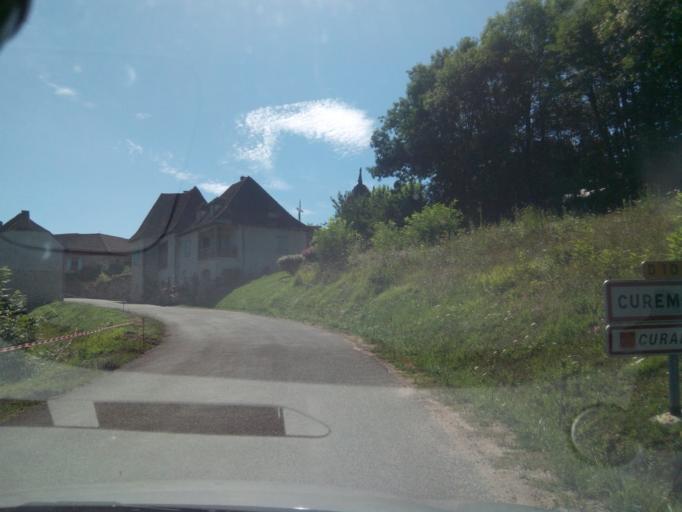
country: FR
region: Midi-Pyrenees
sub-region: Departement du Lot
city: Vayrac
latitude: 45.0037
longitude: 1.7427
